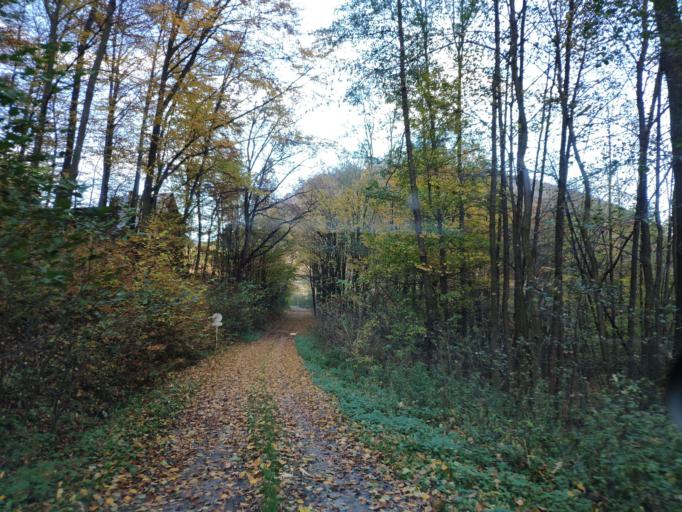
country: SK
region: Presovsky
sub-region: Okres Presov
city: Presov
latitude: 48.8504
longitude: 21.1655
